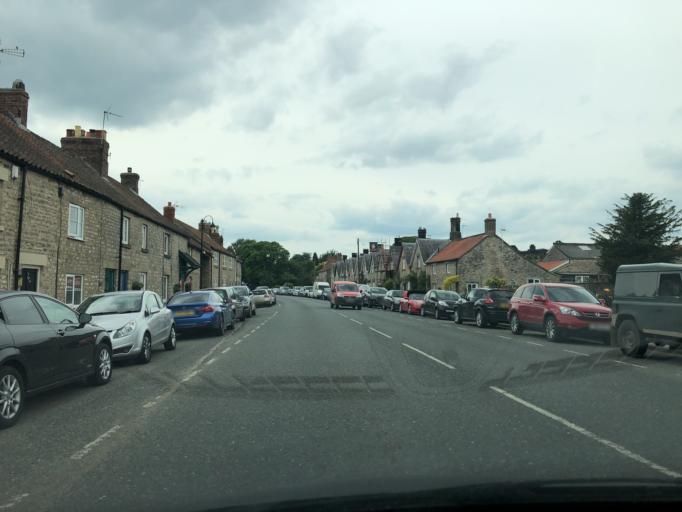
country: GB
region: England
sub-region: North Yorkshire
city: Helmsley
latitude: 54.2474
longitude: -1.0566
